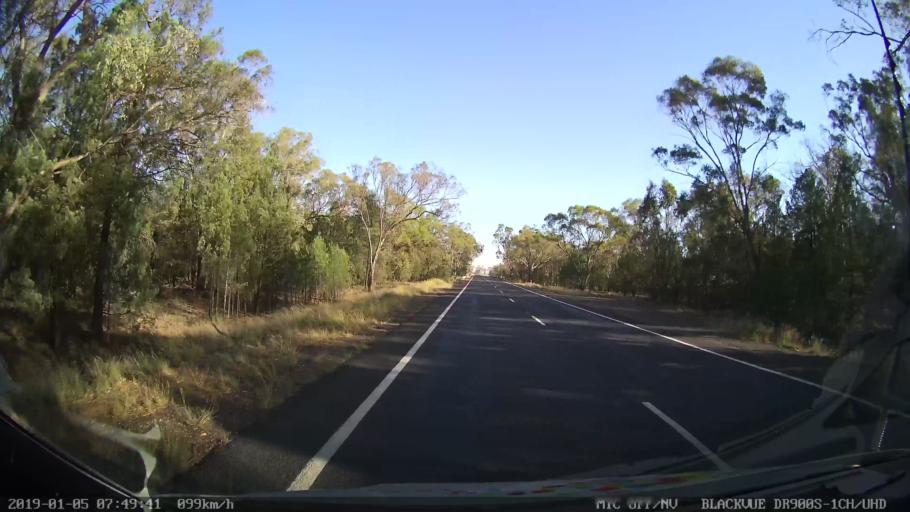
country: AU
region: New South Wales
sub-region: Gilgandra
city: Gilgandra
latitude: -31.7980
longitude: 148.6361
